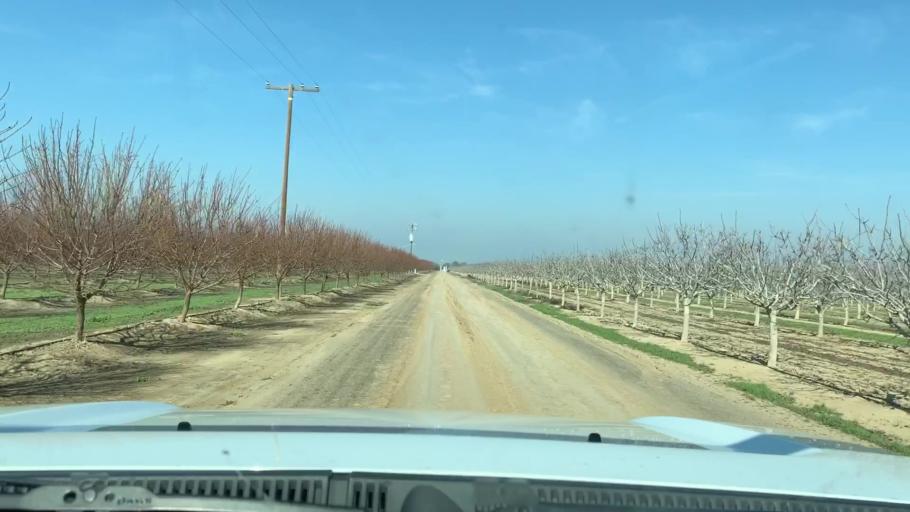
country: US
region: California
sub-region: Kern County
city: Lost Hills
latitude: 35.6105
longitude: -119.5358
